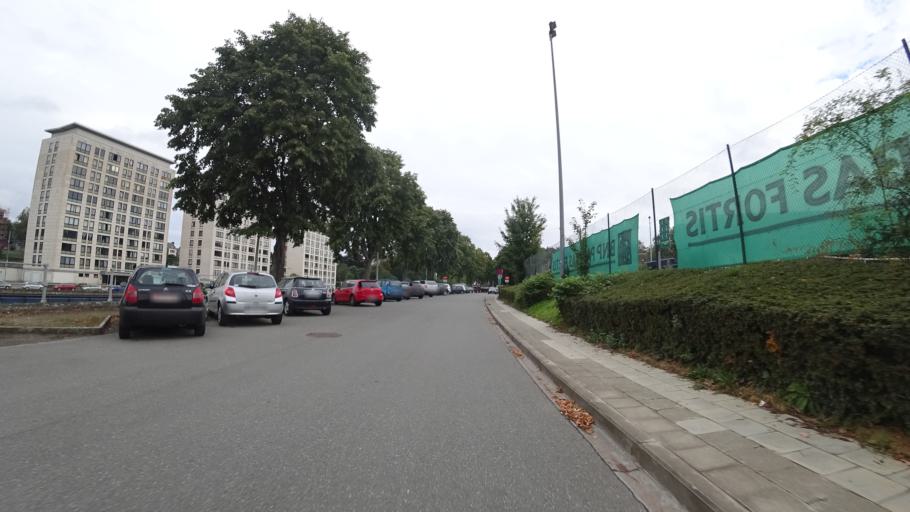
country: BE
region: Wallonia
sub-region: Province de Namur
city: Namur
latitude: 50.4690
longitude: 4.8503
